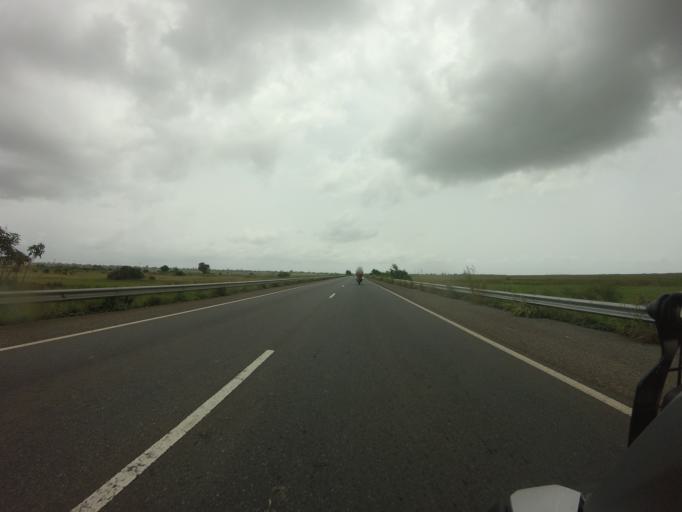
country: GH
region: Volta
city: Keta
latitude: 6.0628
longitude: 0.9269
